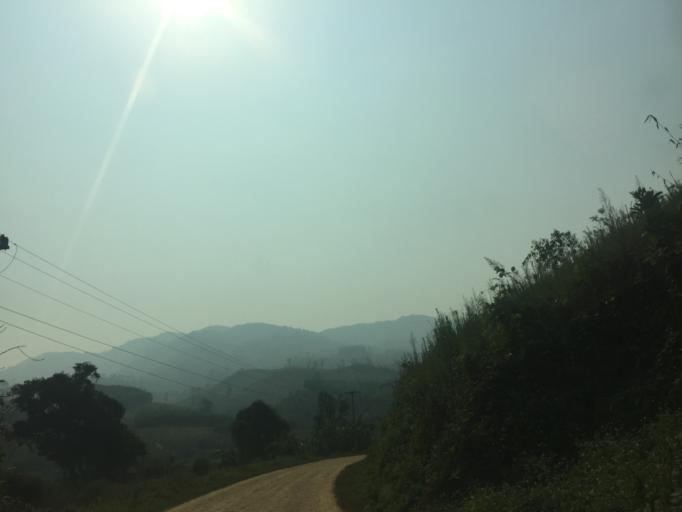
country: TH
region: Phayao
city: Phu Sang
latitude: 19.6714
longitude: 100.5253
